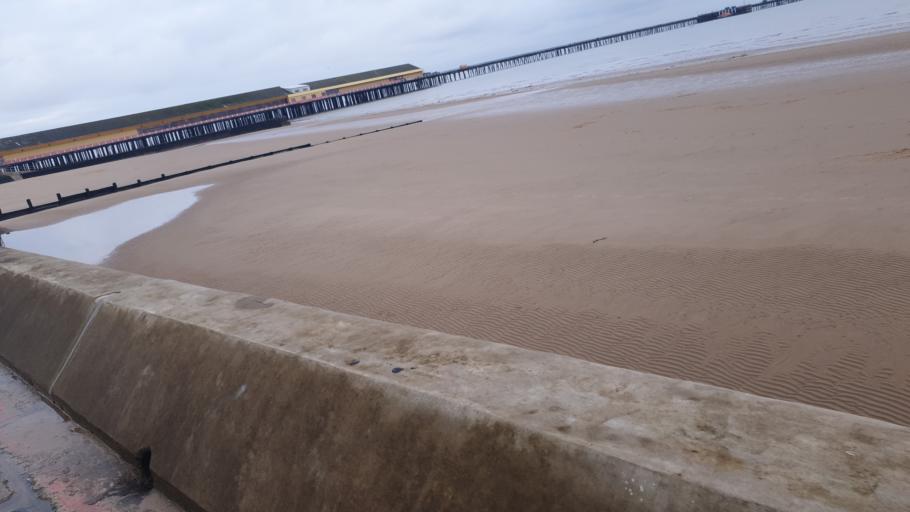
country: GB
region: England
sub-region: Essex
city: Walton-on-the-Naze
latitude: 51.8447
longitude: 1.2685
